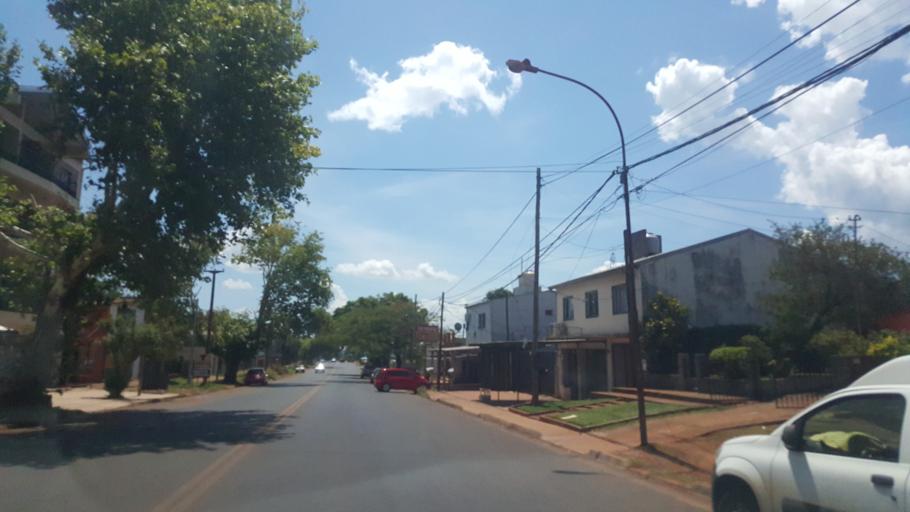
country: AR
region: Misiones
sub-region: Departamento de Capital
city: Posadas
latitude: -27.3680
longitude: -55.9247
